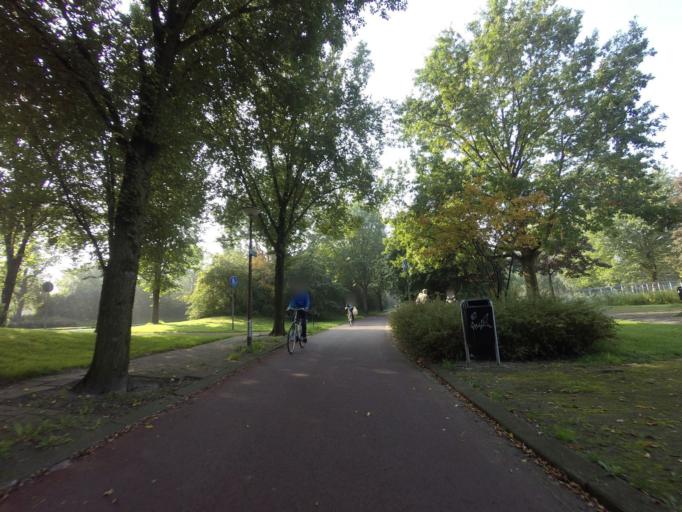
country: NL
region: North Holland
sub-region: Gemeente Alkmaar
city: Alkmaar
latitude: 52.6526
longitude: 4.7581
